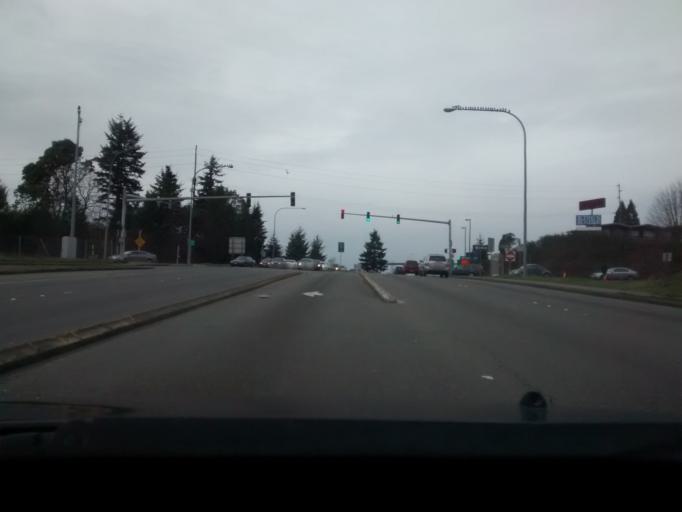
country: US
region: Washington
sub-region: King County
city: Des Moines
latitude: 47.3919
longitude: -122.2915
